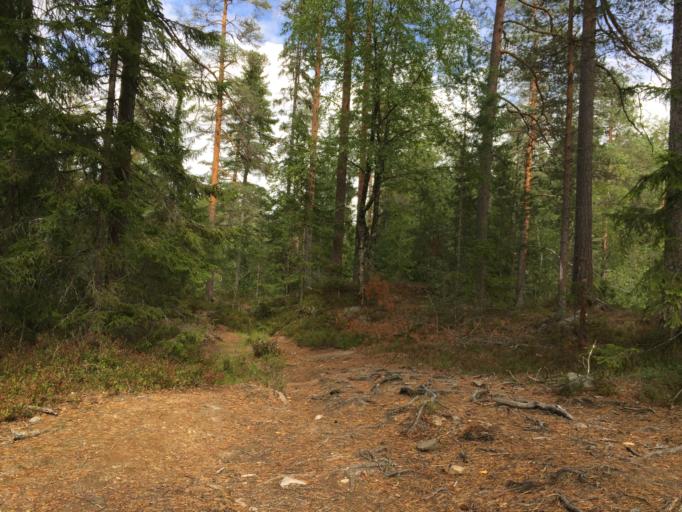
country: NO
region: Akershus
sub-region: Raelingen
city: Fjerdingby
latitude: 59.9088
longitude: 11.0336
